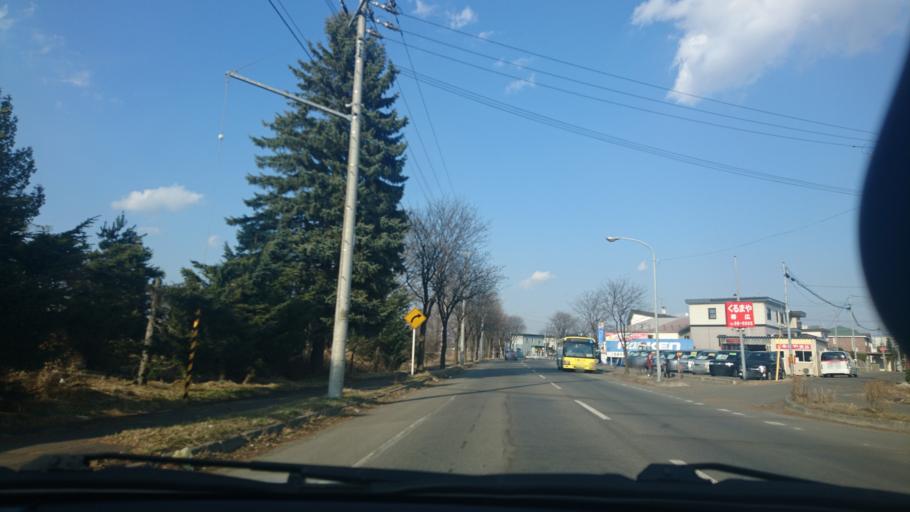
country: JP
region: Hokkaido
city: Obihiro
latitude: 42.9246
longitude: 143.1604
